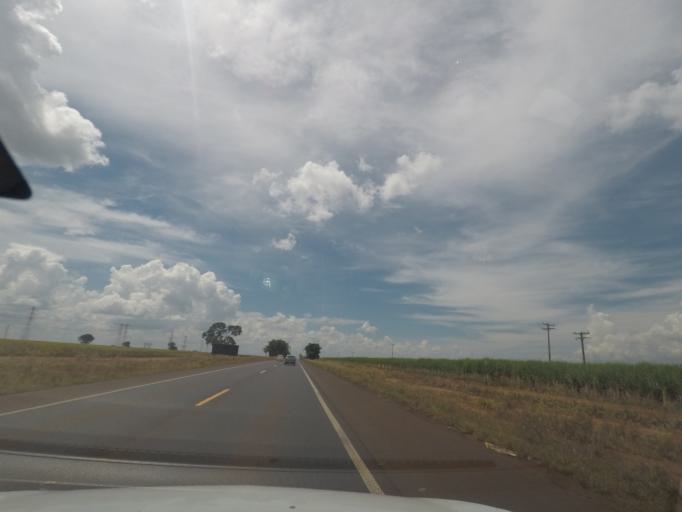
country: BR
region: Sao Paulo
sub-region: Barretos
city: Barretos
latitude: -20.2792
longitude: -48.6715
